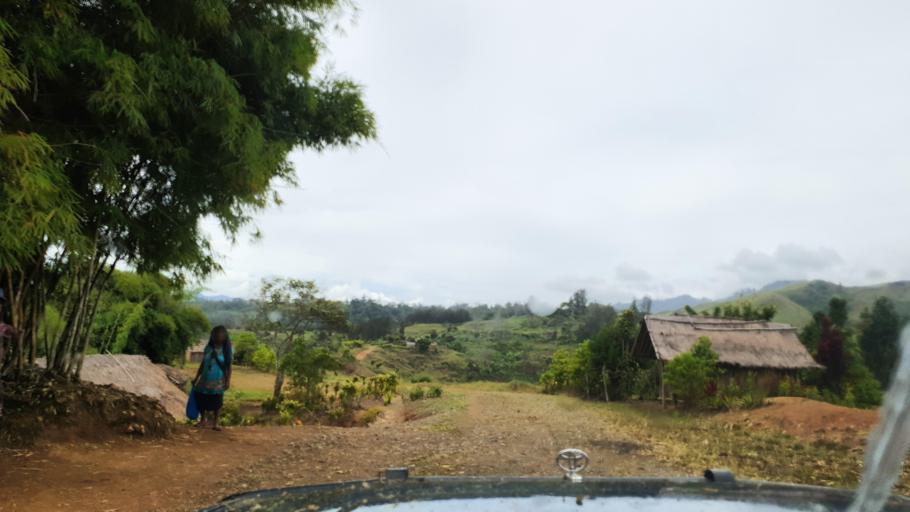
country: PG
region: Jiwaka
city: Minj
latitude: -5.9506
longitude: 144.7727
